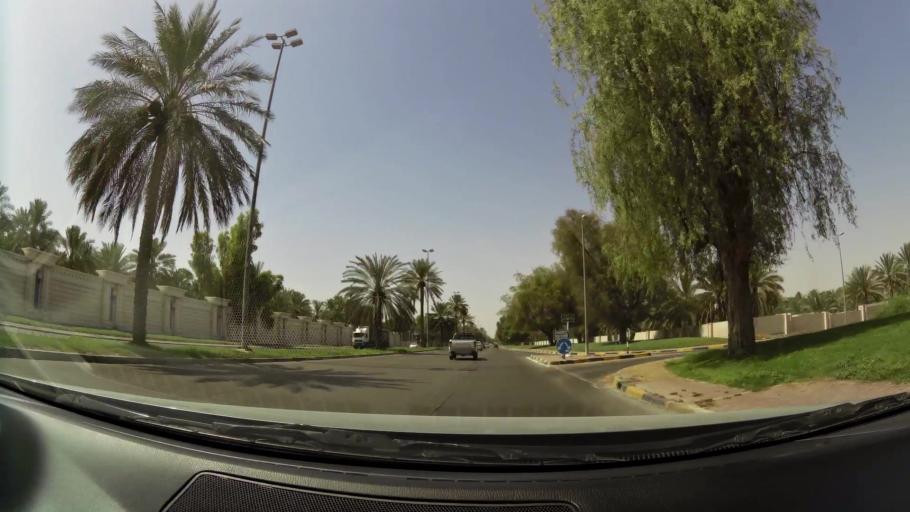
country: OM
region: Al Buraimi
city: Al Buraymi
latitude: 24.2949
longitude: 55.7678
